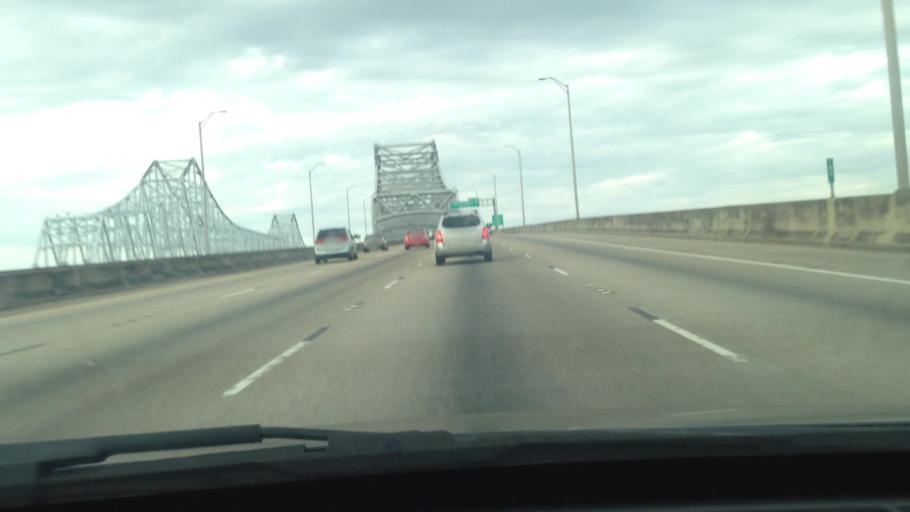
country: US
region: Louisiana
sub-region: Jefferson Parish
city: Gretna
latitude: 29.9389
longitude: -90.0486
